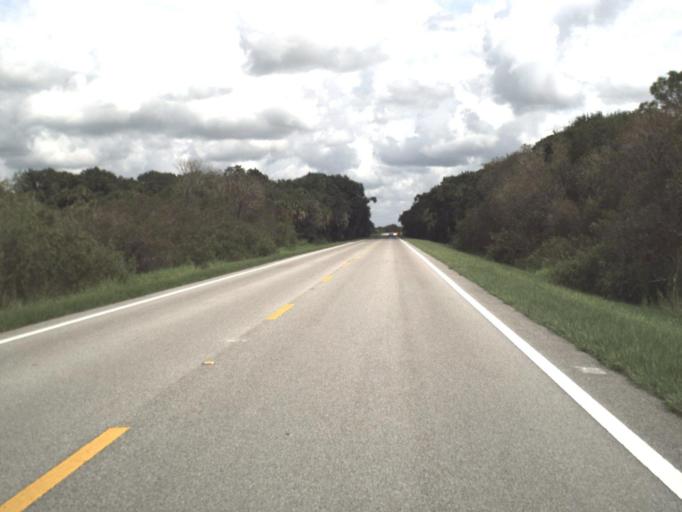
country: US
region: Florida
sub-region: Sarasota County
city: Warm Mineral Springs
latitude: 27.1956
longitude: -82.2103
